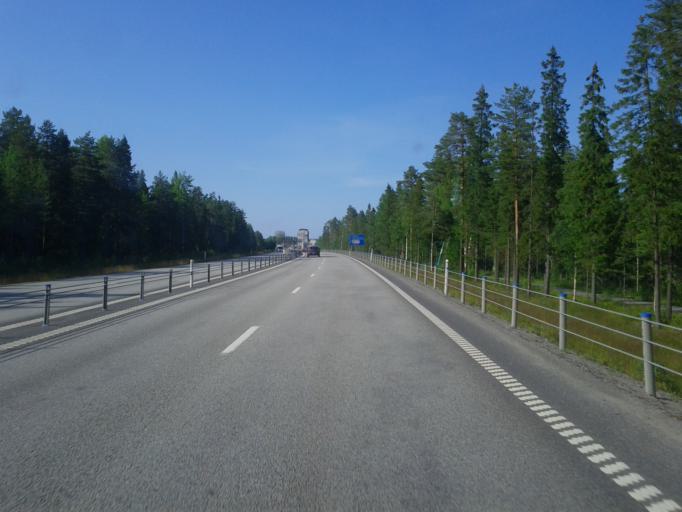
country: SE
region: Vaesterbotten
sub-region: Umea Kommun
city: Ersmark
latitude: 63.8232
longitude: 20.3306
